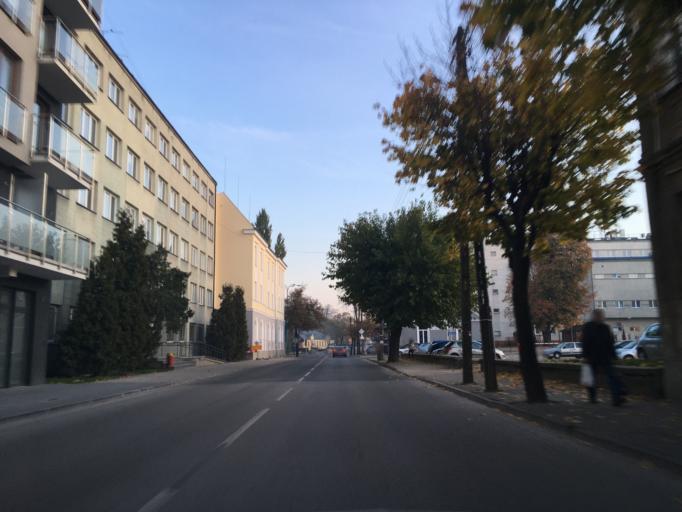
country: PL
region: Lodz Voivodeship
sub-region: Skierniewice
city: Skierniewice
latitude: 51.9596
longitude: 20.1450
